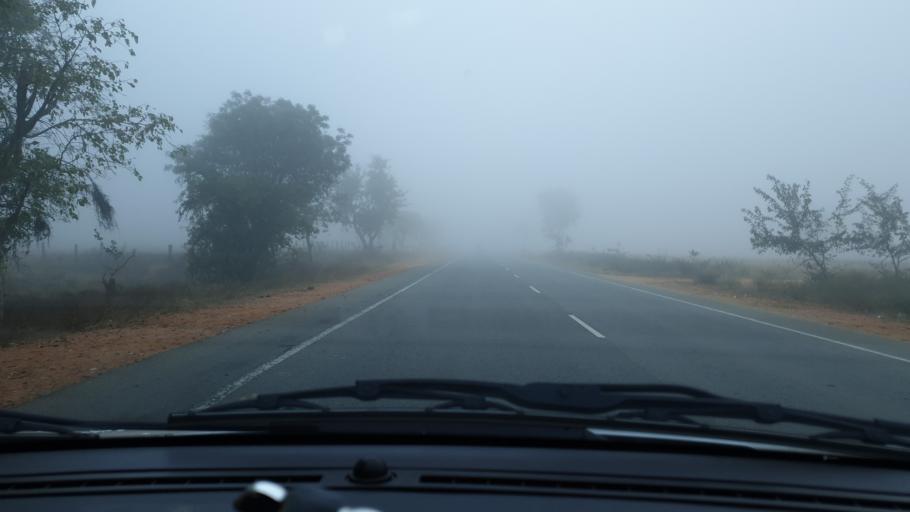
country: IN
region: Telangana
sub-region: Mahbubnagar
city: Nagar Karnul
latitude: 16.6960
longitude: 78.5174
